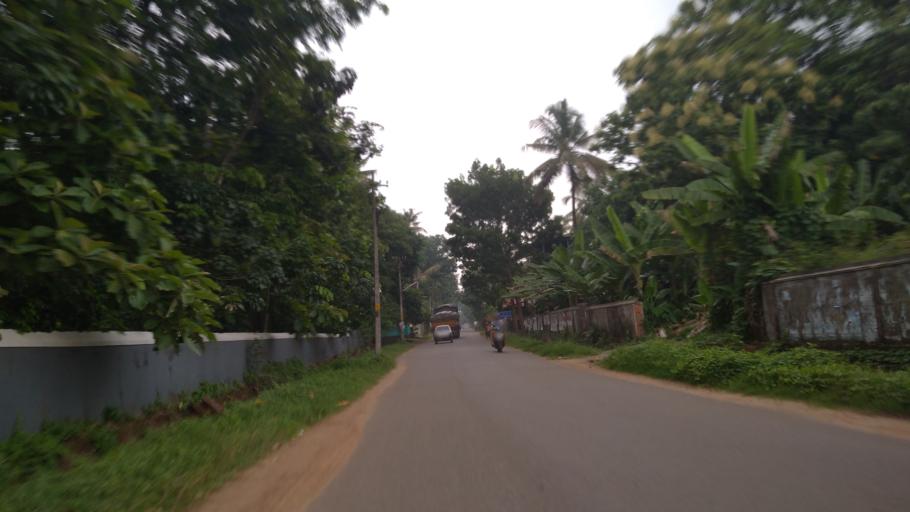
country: IN
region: Kerala
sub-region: Ernakulam
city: Perumbavoor
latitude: 10.0860
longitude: 76.5034
